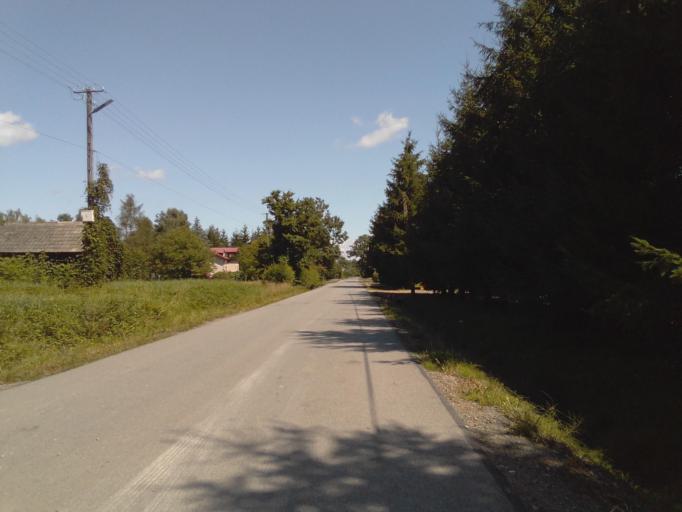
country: PL
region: Subcarpathian Voivodeship
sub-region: Powiat krosnienski
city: Jedlicze
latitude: 49.7494
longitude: 21.6376
